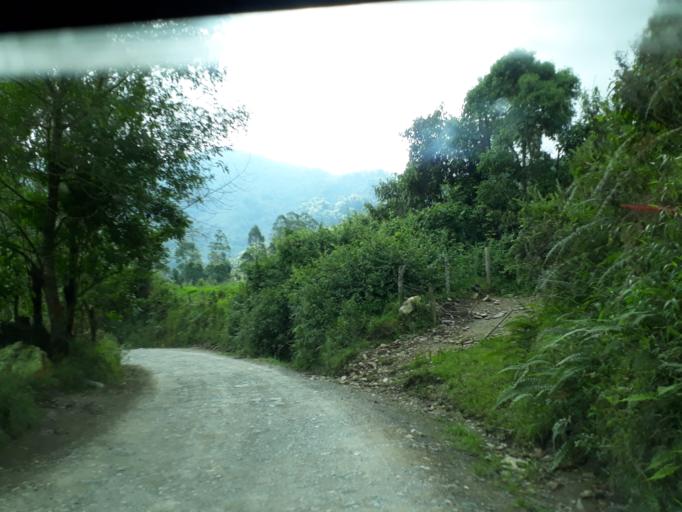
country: CO
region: Cundinamarca
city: Pacho
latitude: 5.2315
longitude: -74.1854
